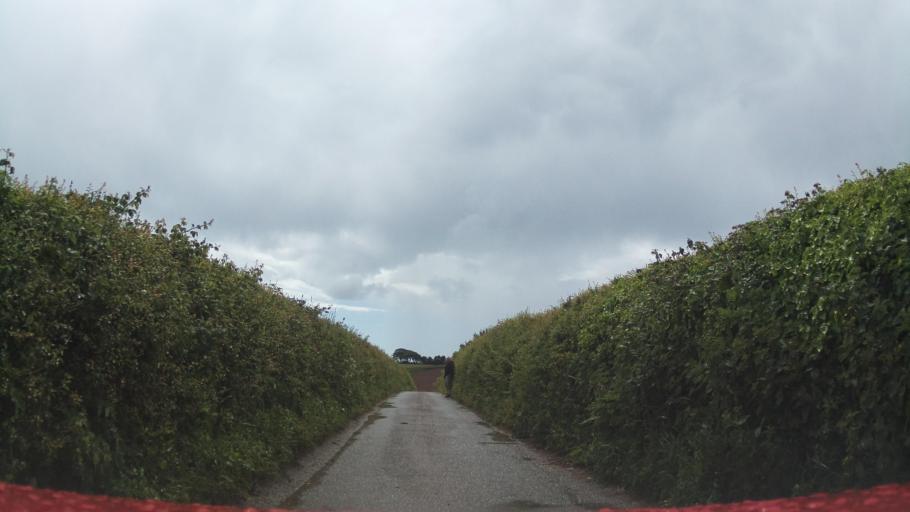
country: GB
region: England
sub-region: Devon
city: Dartmouth
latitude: 50.3555
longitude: -3.5411
